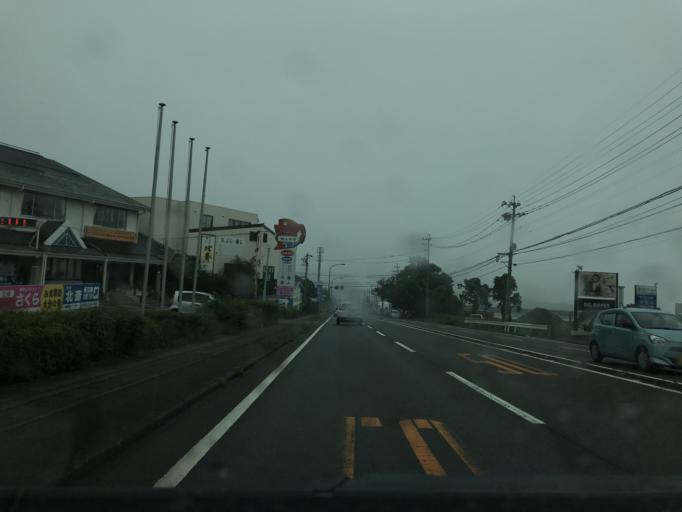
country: JP
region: Oita
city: Beppu
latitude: 33.3017
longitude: 131.4613
